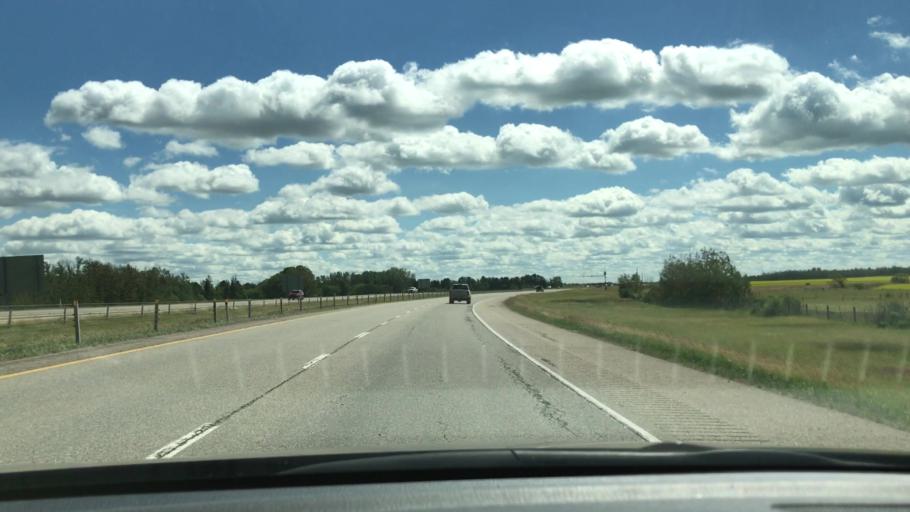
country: CA
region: Alberta
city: Leduc
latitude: 53.2436
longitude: -113.5622
